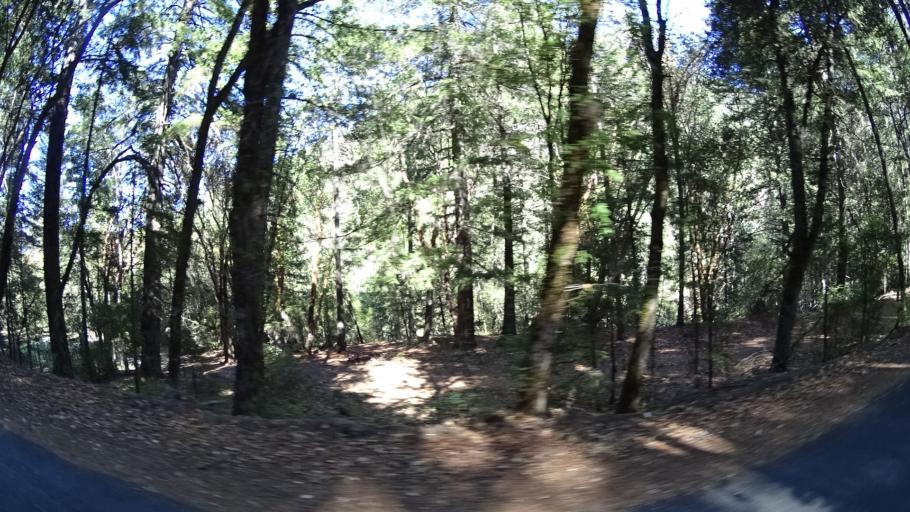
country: US
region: California
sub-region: Humboldt County
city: Willow Creek
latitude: 41.2984
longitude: -123.3645
